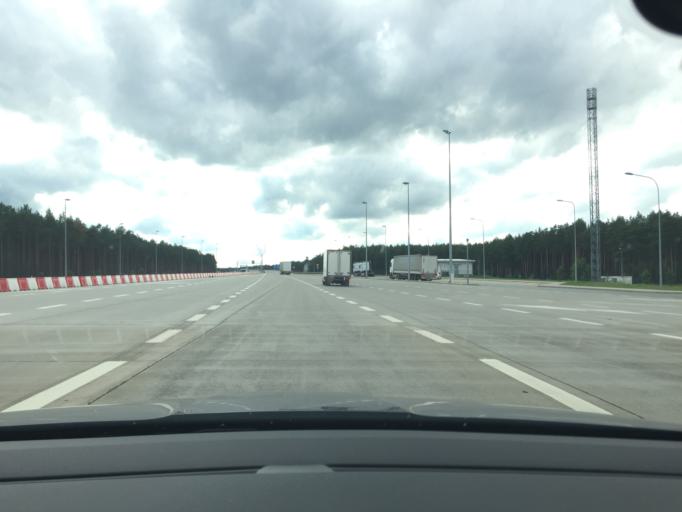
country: PL
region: Lubusz
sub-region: Powiat slubicki
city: Rzepin
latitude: 52.3350
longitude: 14.9032
